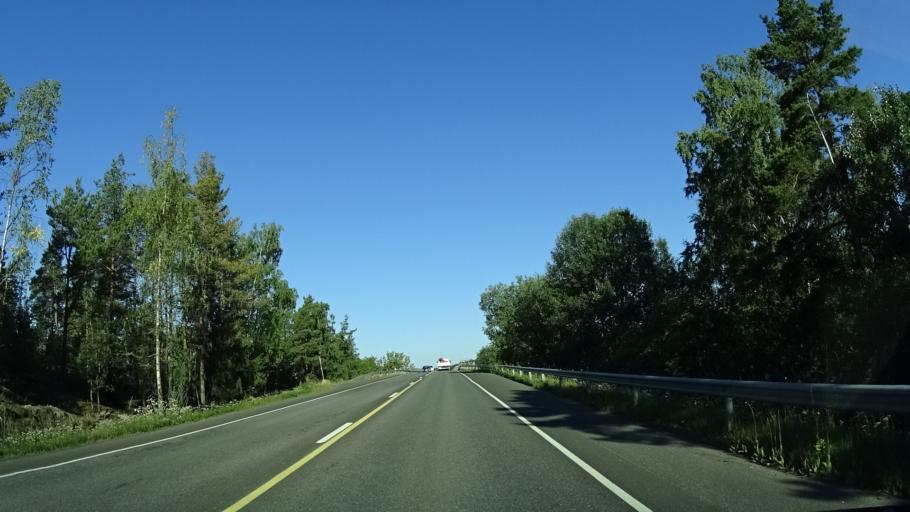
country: FI
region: Varsinais-Suomi
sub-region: Turku
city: Merimasku
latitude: 60.4609
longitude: 21.9320
